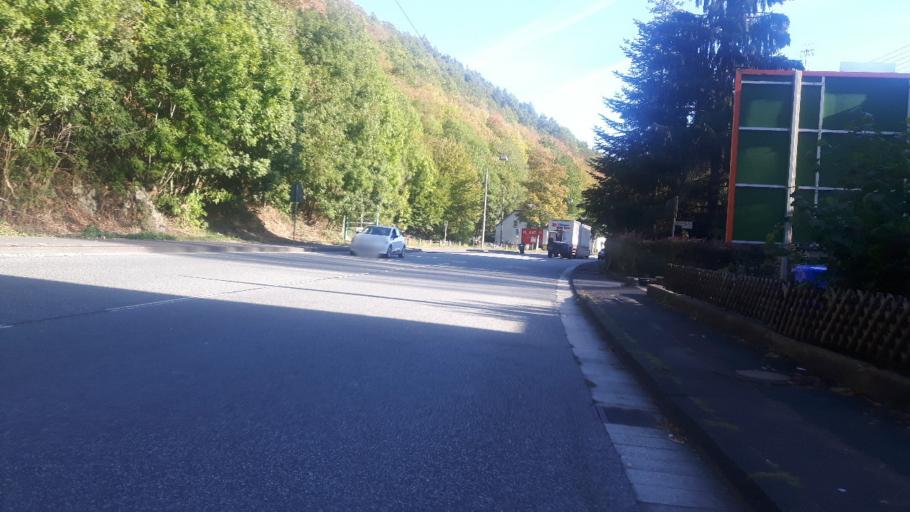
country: DE
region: Rheinland-Pfalz
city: Betzdorf
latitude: 50.8007
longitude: 7.8595
